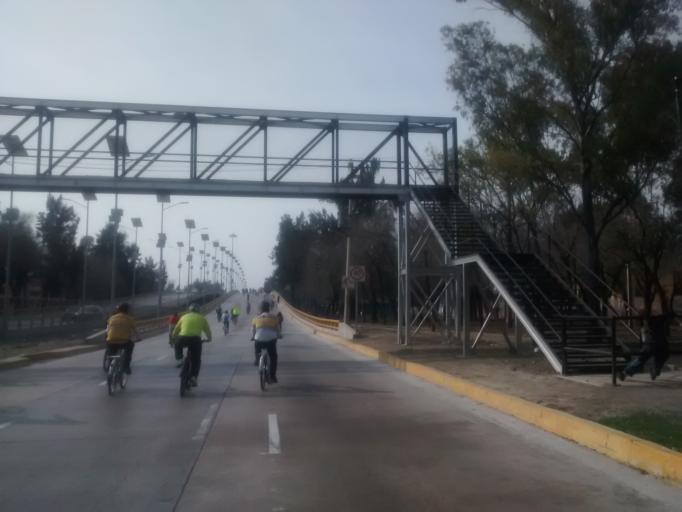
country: MX
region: Mexico City
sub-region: Iztacalco
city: Iztacalco
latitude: 19.3881
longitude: -99.1001
